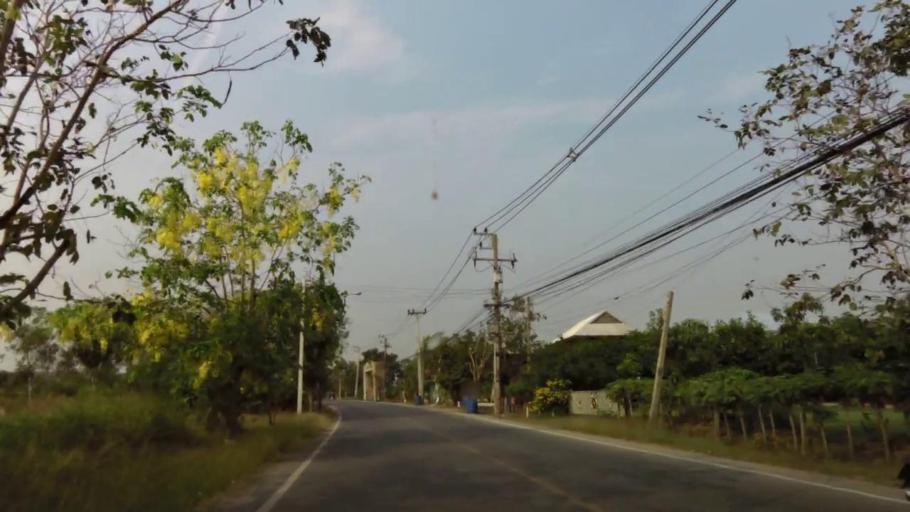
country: TH
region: Phra Nakhon Si Ayutthaya
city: Phra Nakhon Si Ayutthaya
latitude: 14.3408
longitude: 100.5743
